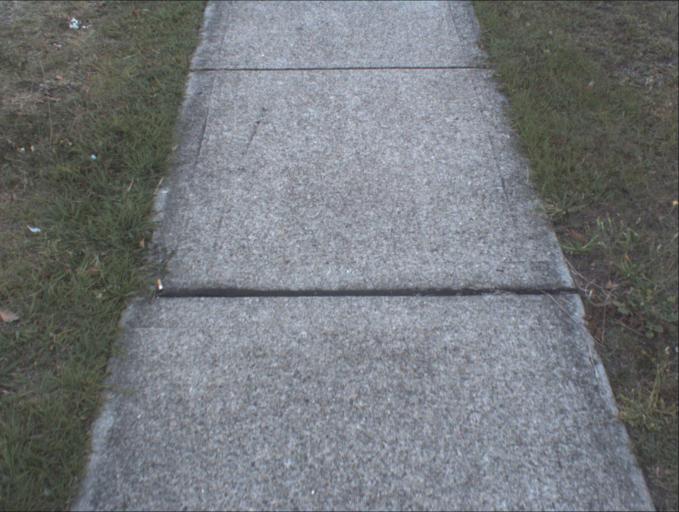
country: AU
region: Queensland
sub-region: Gold Coast
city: Yatala
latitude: -27.7088
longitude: 153.2129
